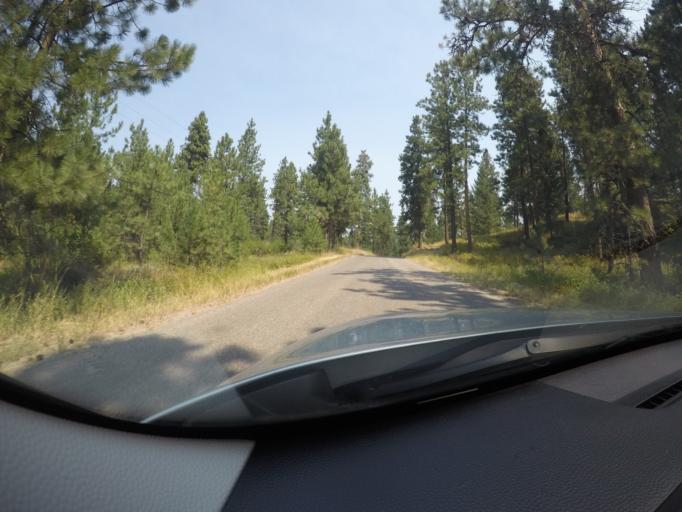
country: US
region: Montana
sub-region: Lake County
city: Polson
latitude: 47.7632
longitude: -114.1599
